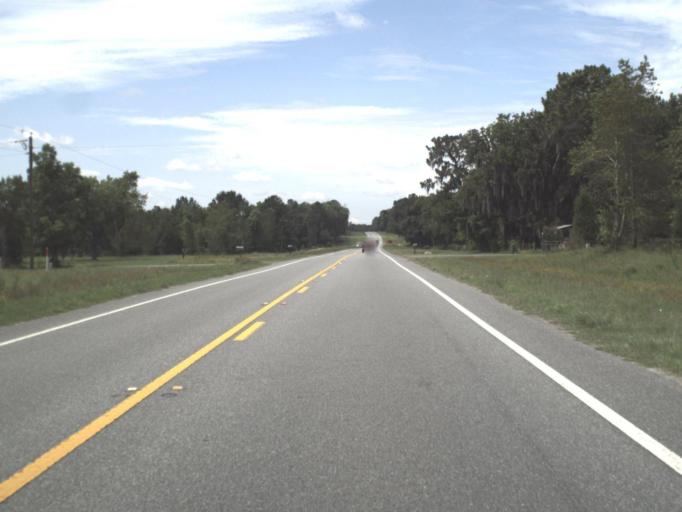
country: US
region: Florida
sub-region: Suwannee County
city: Live Oak
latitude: 30.3757
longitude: -82.9393
